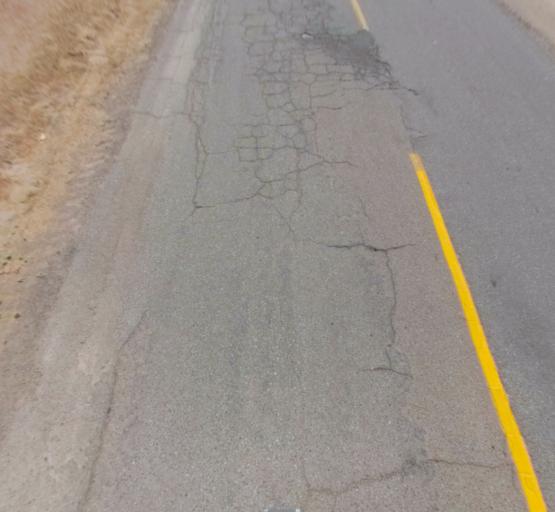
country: US
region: California
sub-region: Madera County
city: Bonadelle Ranchos-Madera Ranchos
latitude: 36.8949
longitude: -119.8412
